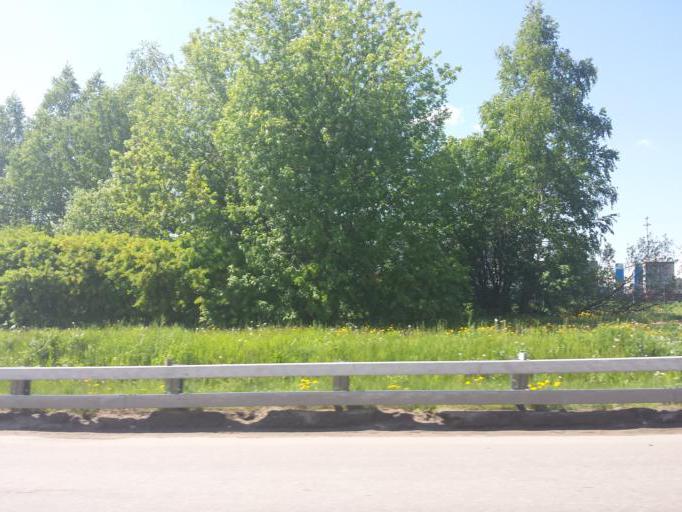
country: RU
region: Moscow
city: Lianozovo
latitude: 55.9133
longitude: 37.5908
